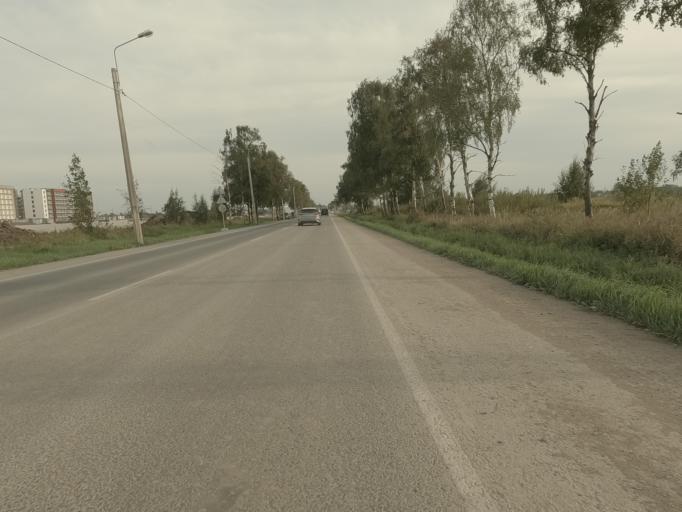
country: RU
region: St.-Petersburg
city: Strel'na
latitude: 59.8447
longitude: 30.0910
